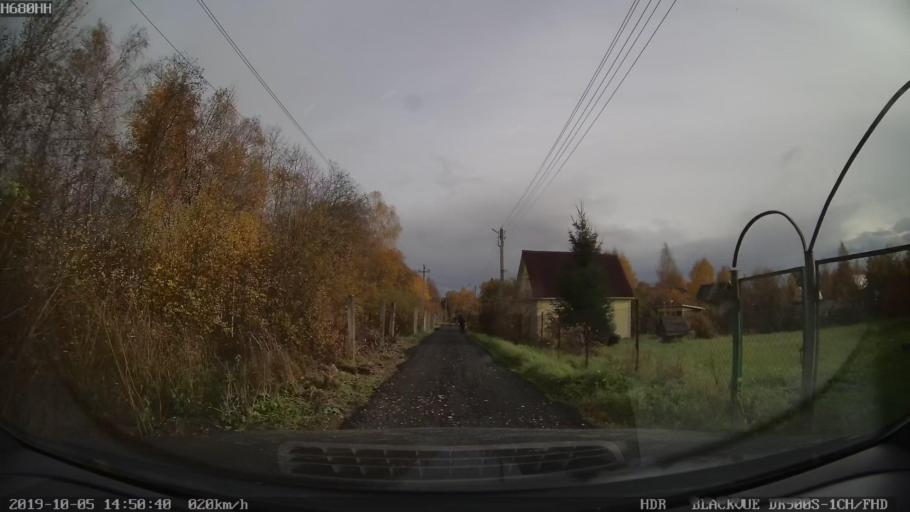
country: RU
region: Moskovskaya
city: Solnechnogorsk
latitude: 56.2140
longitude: 36.9127
